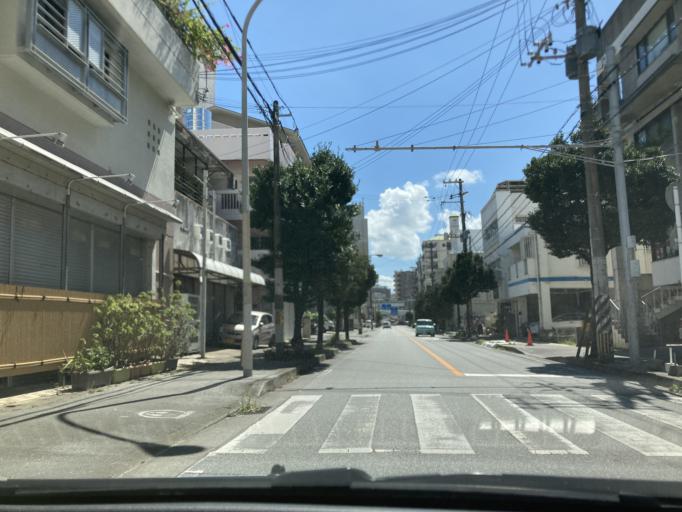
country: JP
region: Okinawa
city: Naha-shi
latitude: 26.2158
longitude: 127.6746
